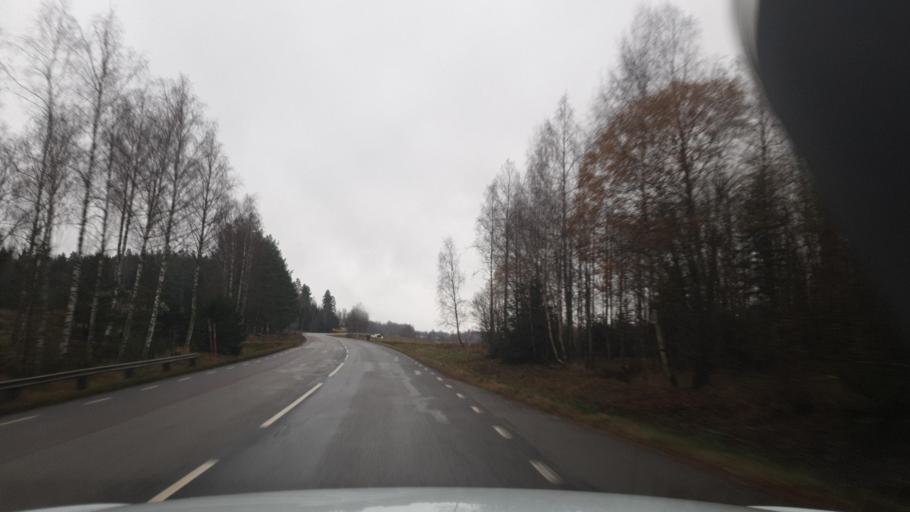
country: SE
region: Vaermland
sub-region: Arvika Kommun
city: Arvika
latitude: 59.7060
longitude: 12.6355
